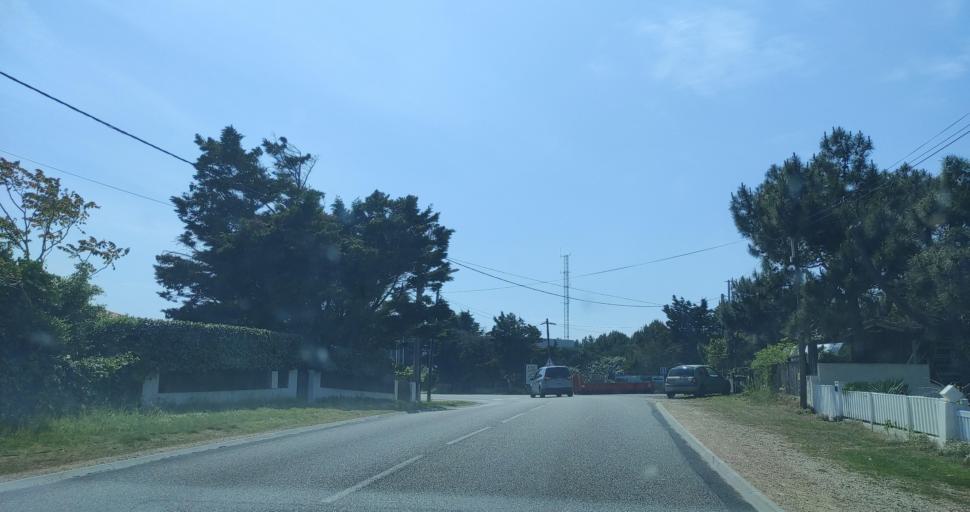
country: FR
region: Aquitaine
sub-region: Departement de la Gironde
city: Arcachon
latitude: 44.6473
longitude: -1.2538
